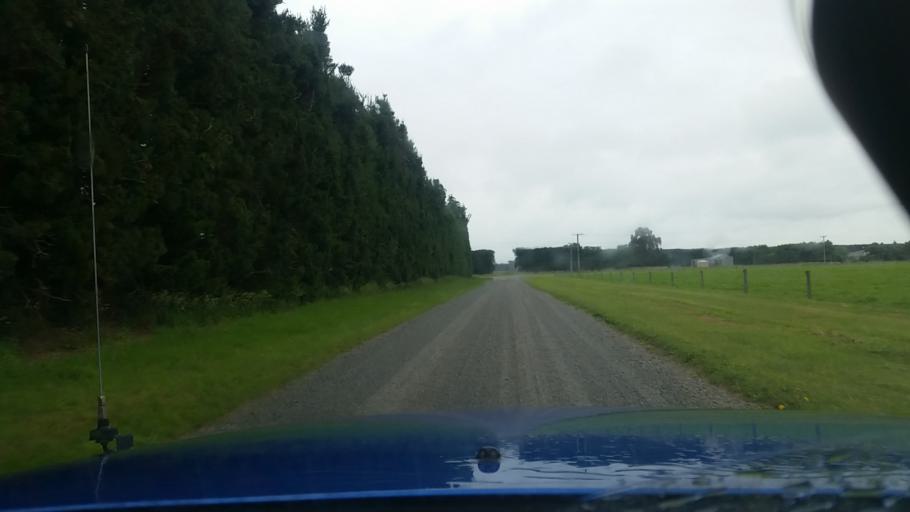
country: NZ
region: Canterbury
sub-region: Ashburton District
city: Tinwald
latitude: -43.9031
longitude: 171.5884
